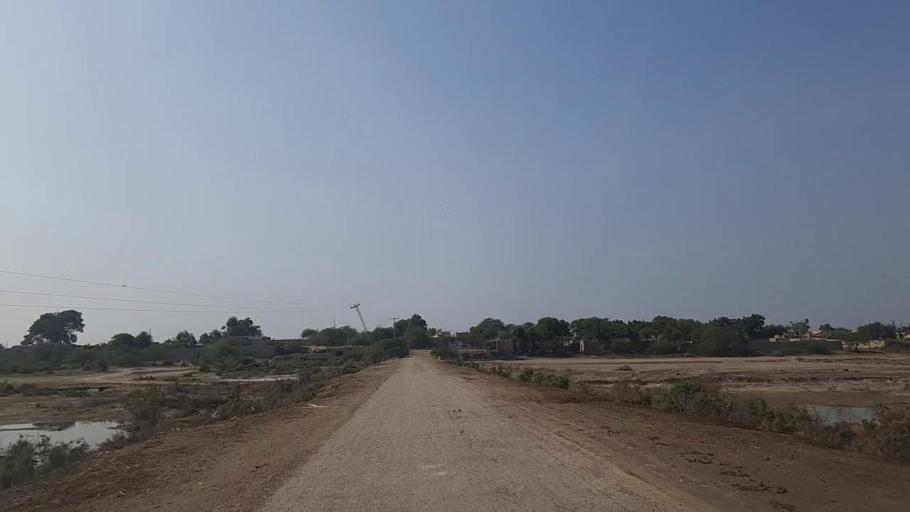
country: PK
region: Sindh
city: Daur
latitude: 26.4895
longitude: 68.4430
